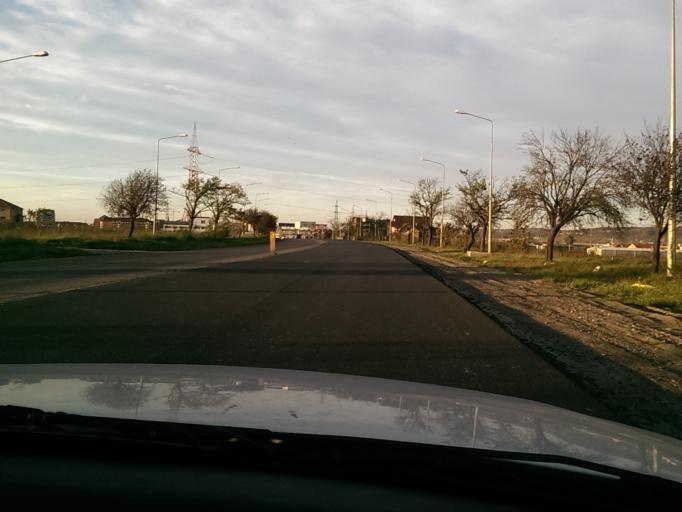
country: RO
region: Bihor
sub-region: Comuna Sanmartin
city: Sanmartin
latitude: 47.0196
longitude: 21.9630
